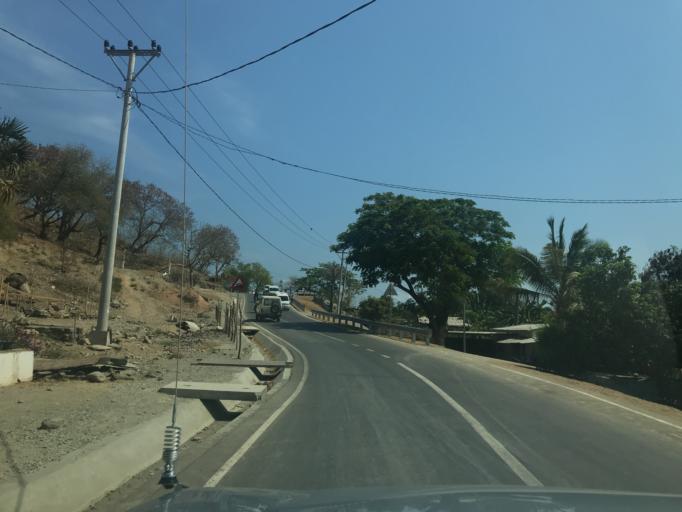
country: TL
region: Dili
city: Dili
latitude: -8.5601
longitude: 125.5228
